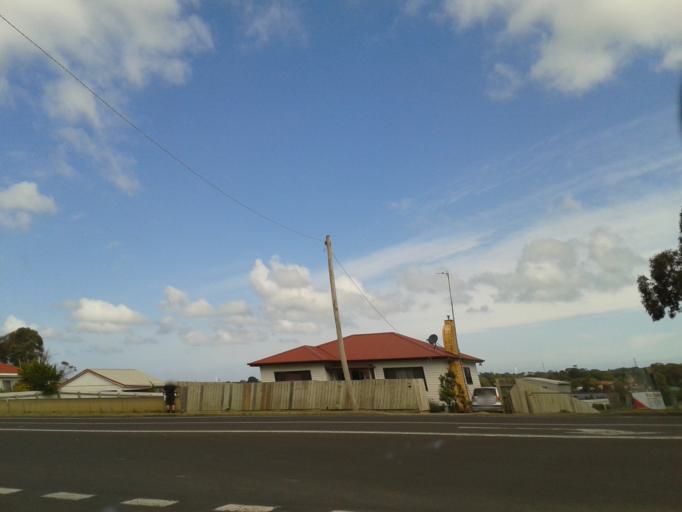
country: AU
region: Victoria
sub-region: Glenelg
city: Portland
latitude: -38.3403
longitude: 141.5888
